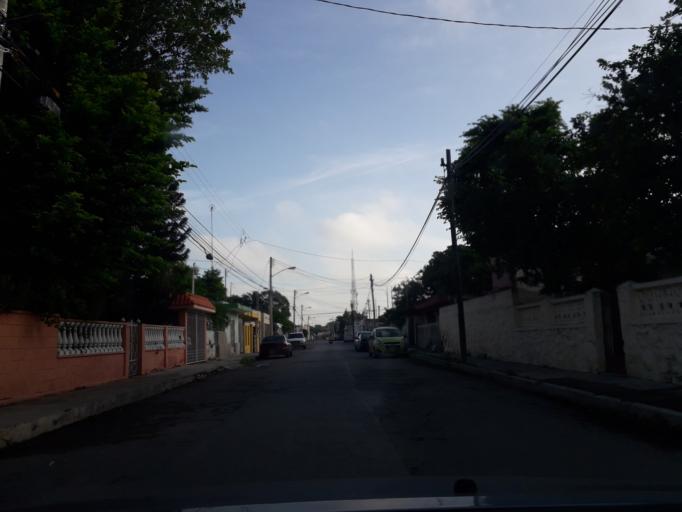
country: MX
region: Yucatan
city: Merida
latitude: 20.9689
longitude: -89.6458
